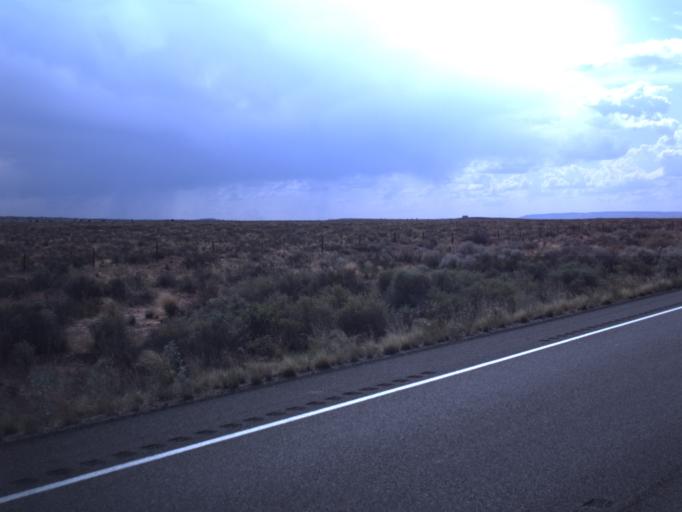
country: US
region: Arizona
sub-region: Coconino County
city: Page
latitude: 37.0935
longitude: -111.7462
